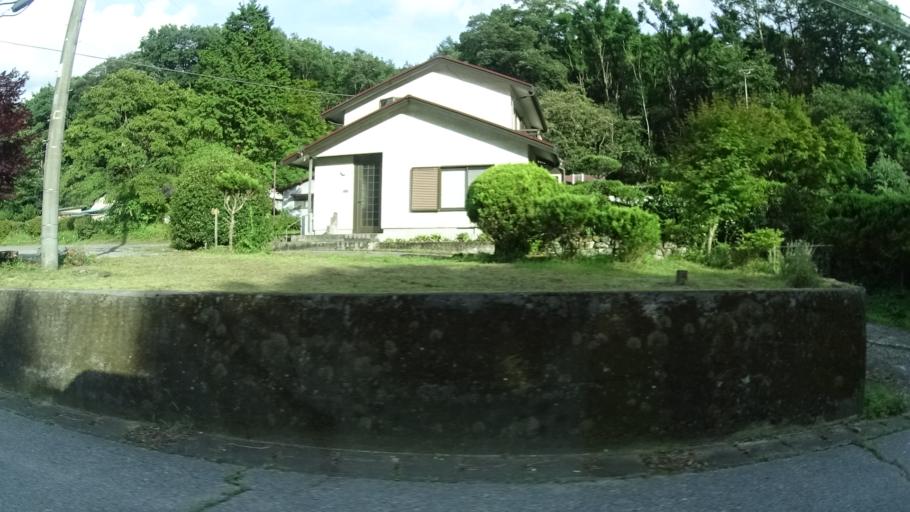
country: JP
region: Tochigi
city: Nikko
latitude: 36.6571
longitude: 139.4564
